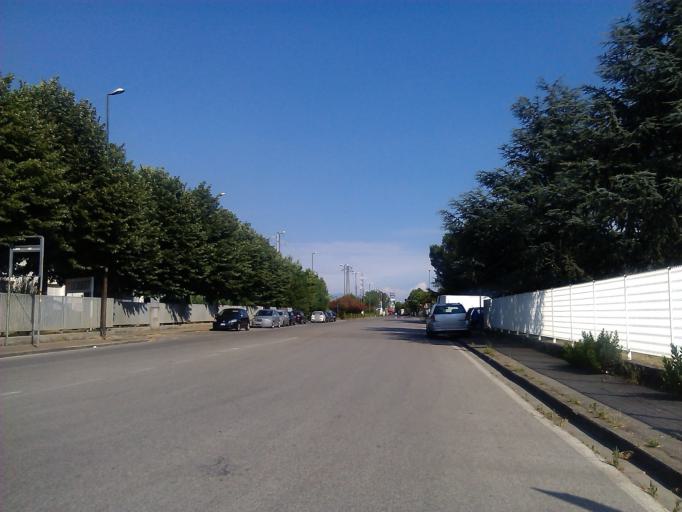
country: IT
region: Tuscany
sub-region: Province of Florence
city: Campi Bisenzio
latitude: 43.8504
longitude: 11.1291
